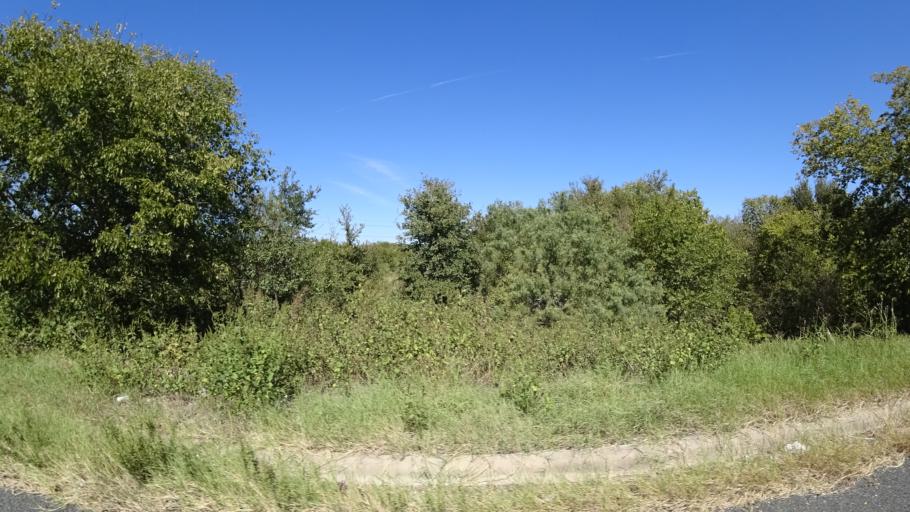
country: US
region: Texas
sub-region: Travis County
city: Austin
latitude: 30.1987
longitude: -97.6897
